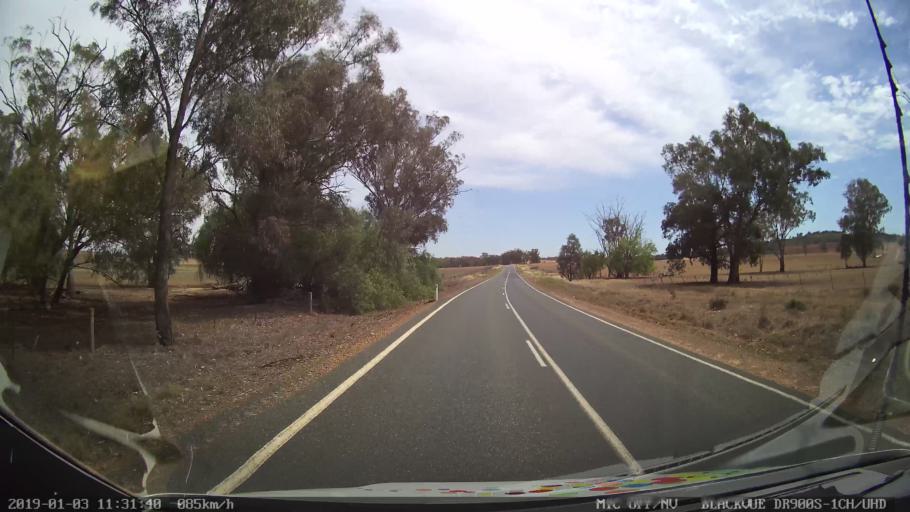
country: AU
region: New South Wales
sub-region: Weddin
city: Grenfell
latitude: -33.9679
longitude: 148.1821
